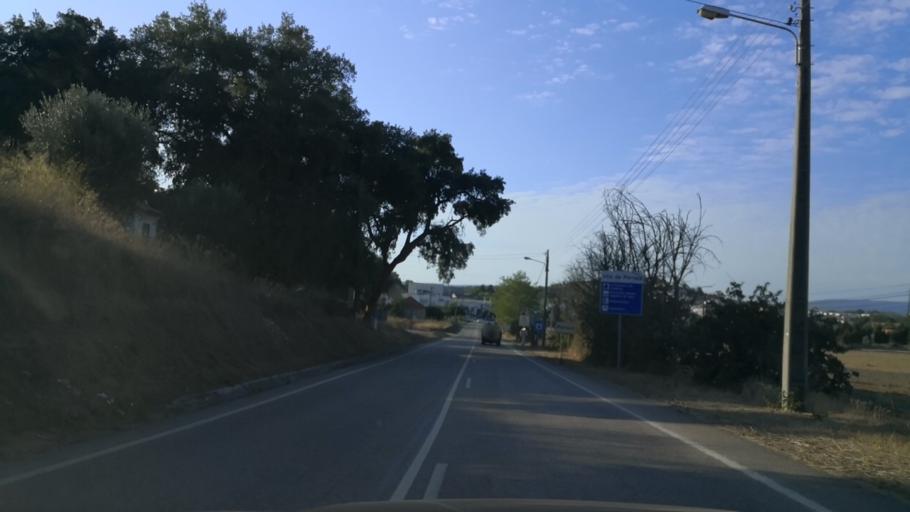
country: PT
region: Santarem
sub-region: Alcanena
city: Alcanena
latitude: 39.3739
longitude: -8.6598
